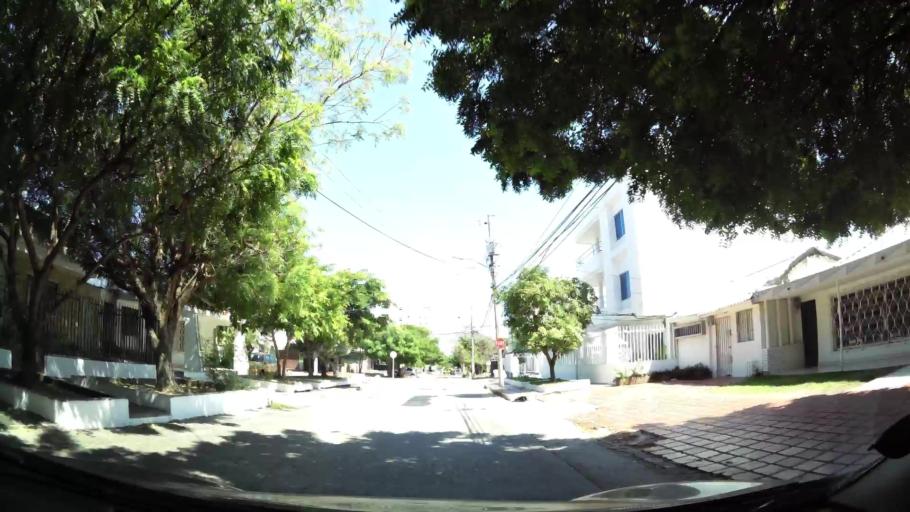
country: CO
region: Atlantico
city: Barranquilla
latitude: 11.0125
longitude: -74.8079
